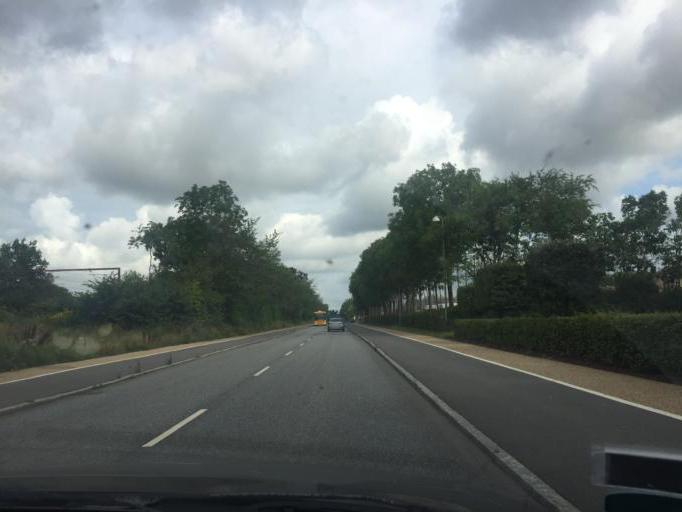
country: DK
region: Capital Region
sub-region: Allerod Kommune
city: Lillerod
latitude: 55.8747
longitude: 12.3541
